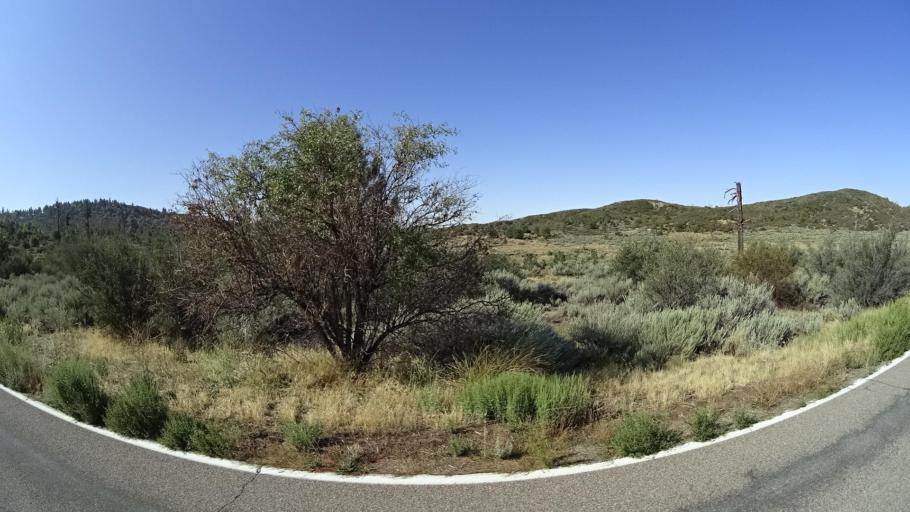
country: US
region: California
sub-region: San Diego County
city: Pine Valley
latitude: 32.9159
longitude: -116.4675
